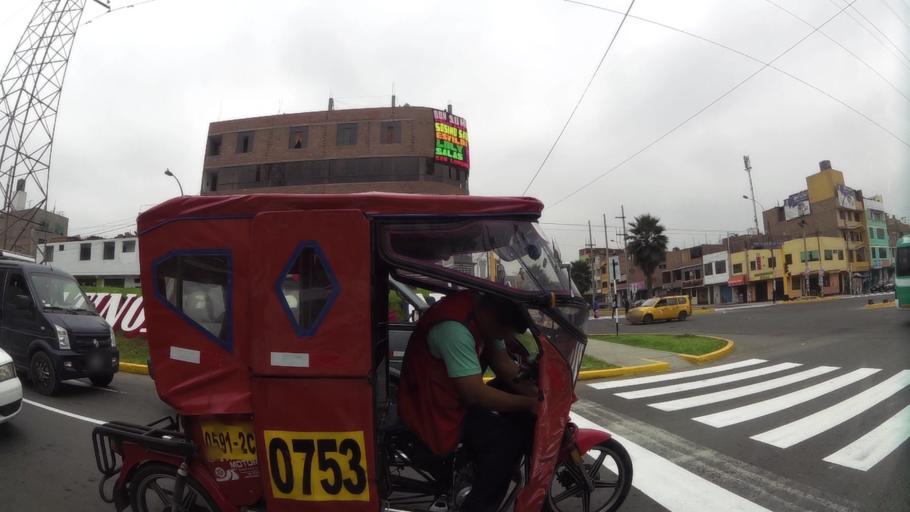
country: PE
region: Lima
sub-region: Lima
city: Independencia
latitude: -11.9700
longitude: -77.0805
